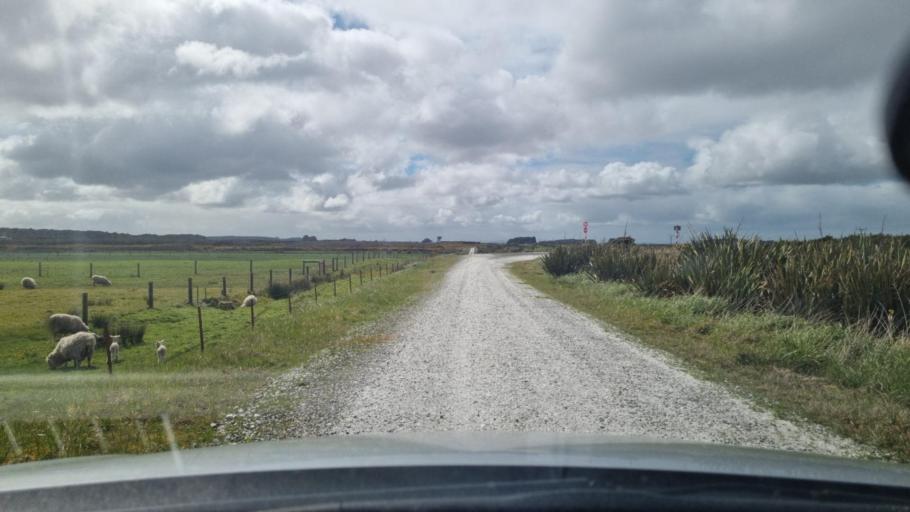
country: NZ
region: Southland
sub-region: Invercargill City
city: Bluff
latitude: -46.5360
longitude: 168.3037
